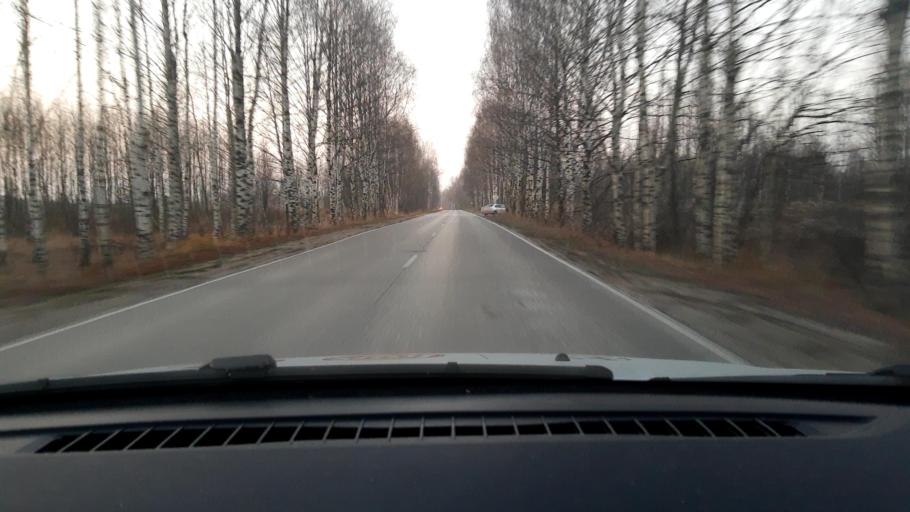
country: RU
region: Nizjnij Novgorod
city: Neklyudovo
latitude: 56.4714
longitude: 43.8873
